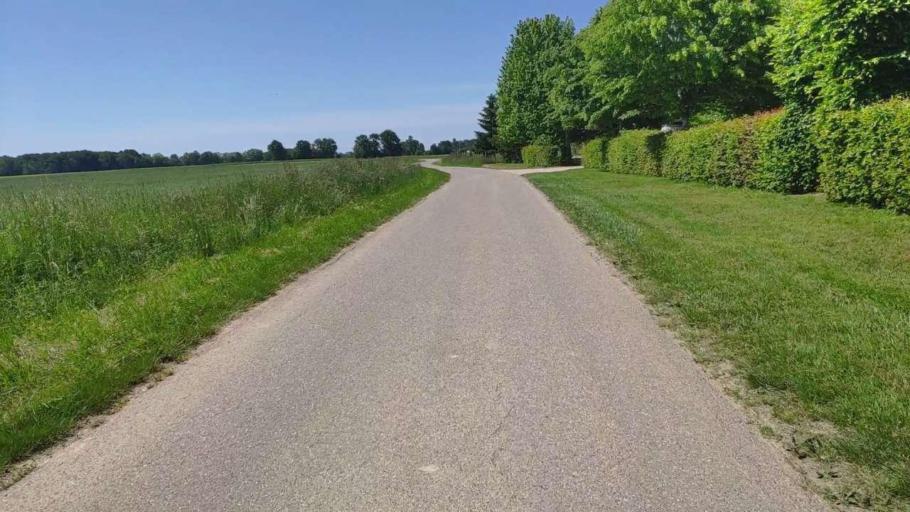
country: FR
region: Franche-Comte
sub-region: Departement du Jura
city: Bletterans
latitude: 46.7733
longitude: 5.4126
